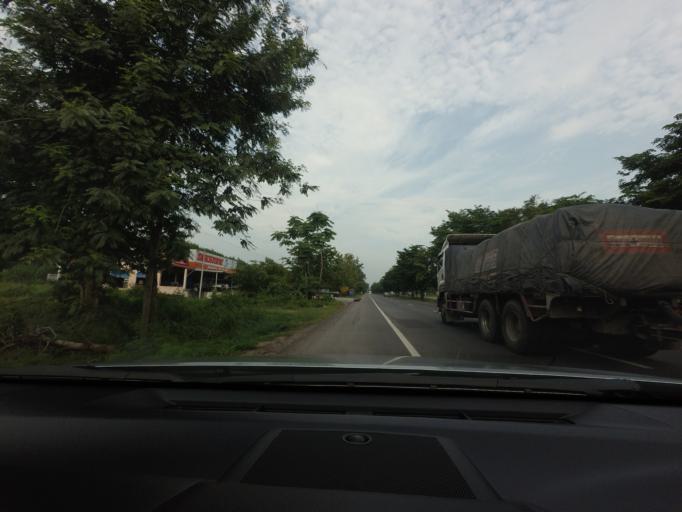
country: TH
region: Surat Thani
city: Ban Na Doem
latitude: 8.9411
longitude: 99.2570
